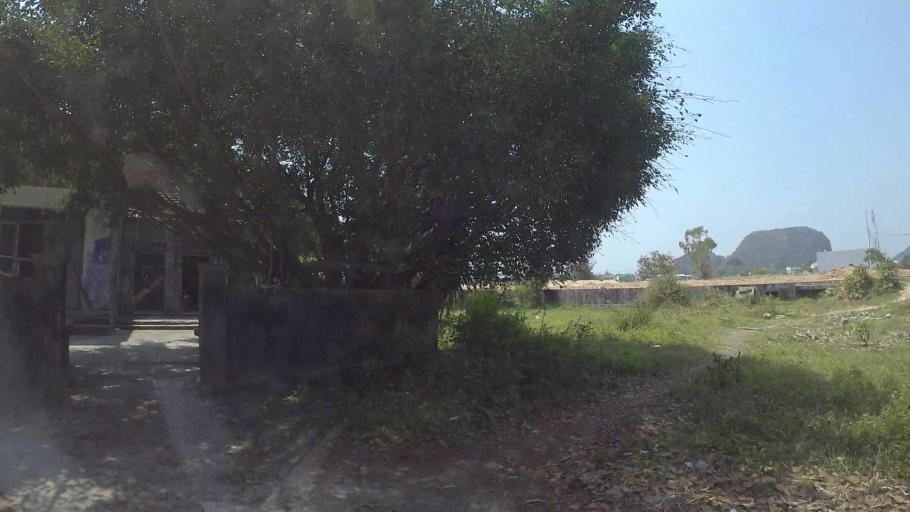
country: VN
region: Da Nang
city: Ngu Hanh Son
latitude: 15.9945
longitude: 108.2624
